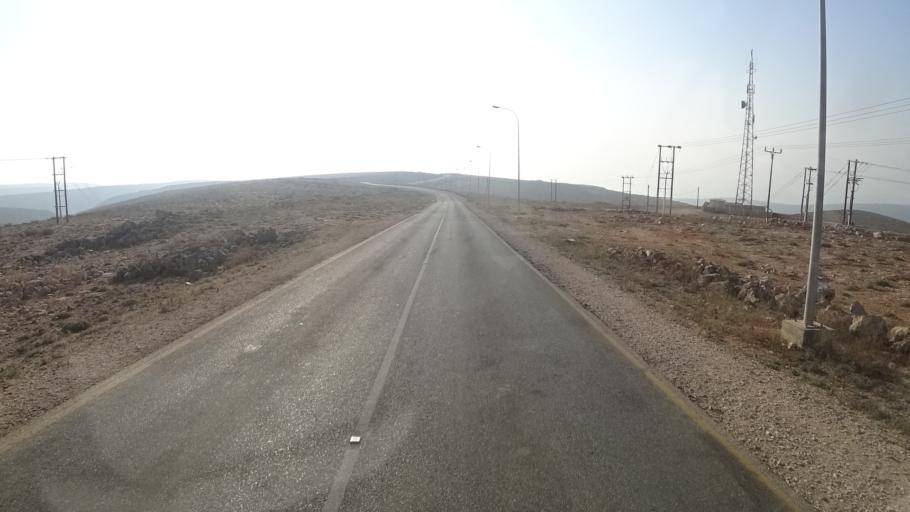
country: YE
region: Al Mahrah
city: Hawf
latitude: 16.7683
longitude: 53.2287
